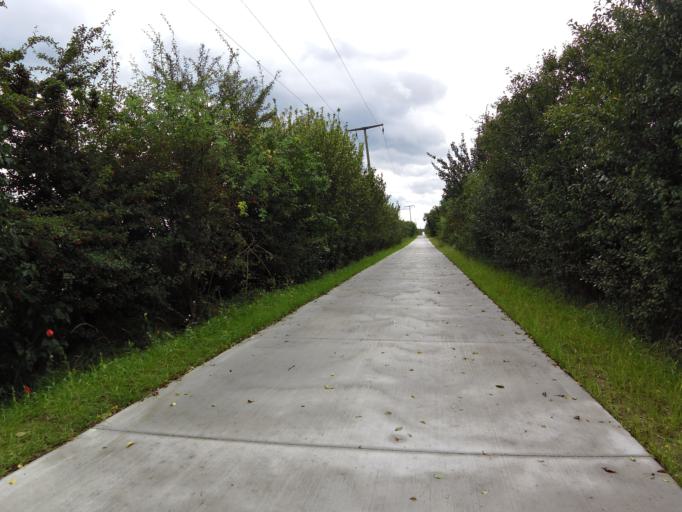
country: DE
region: Saxony-Anhalt
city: Arneburg
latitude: 52.6541
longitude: 12.0040
